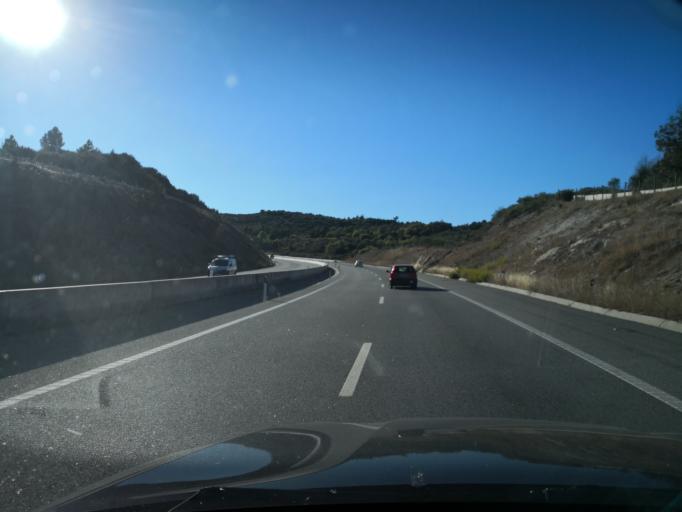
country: PT
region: Vila Real
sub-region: Murca
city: Murca
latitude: 41.3893
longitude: -7.4710
